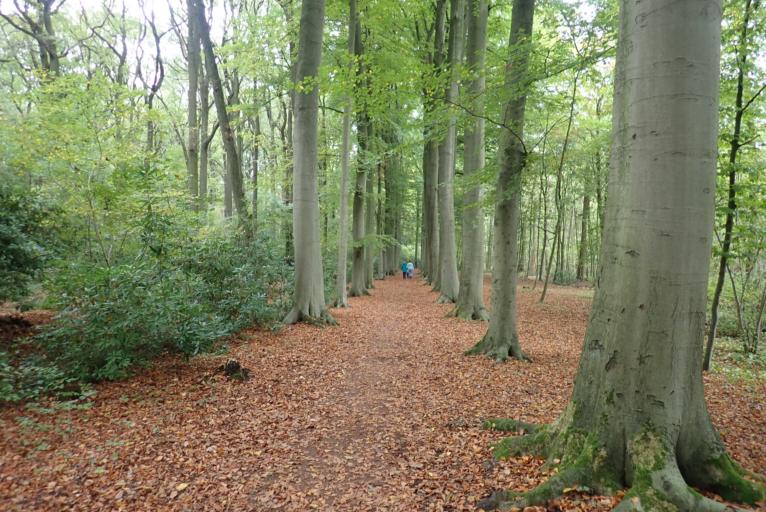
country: BE
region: Flanders
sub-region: Provincie Antwerpen
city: Ranst
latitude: 51.1982
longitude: 4.5529
